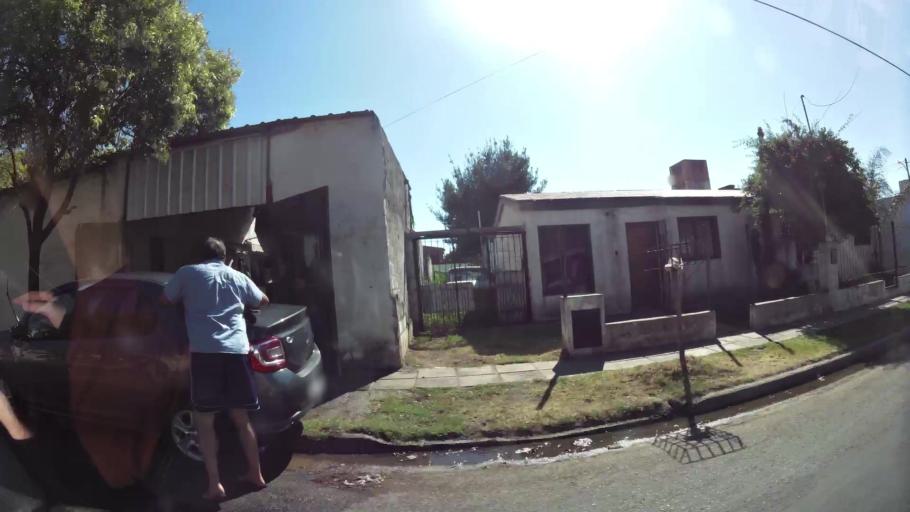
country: AR
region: Cordoba
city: Villa Allende
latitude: -31.3402
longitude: -64.2438
